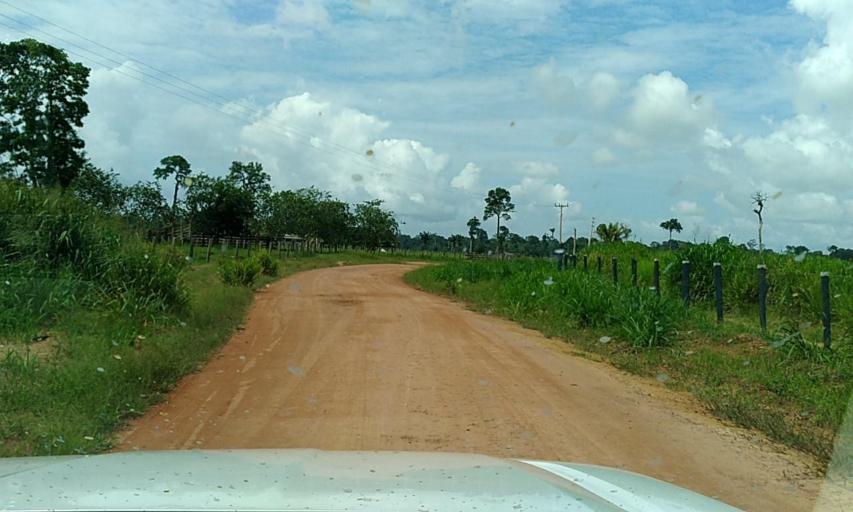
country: BR
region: Para
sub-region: Senador Jose Porfirio
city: Senador Jose Porfirio
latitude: -2.5192
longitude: -51.8495
